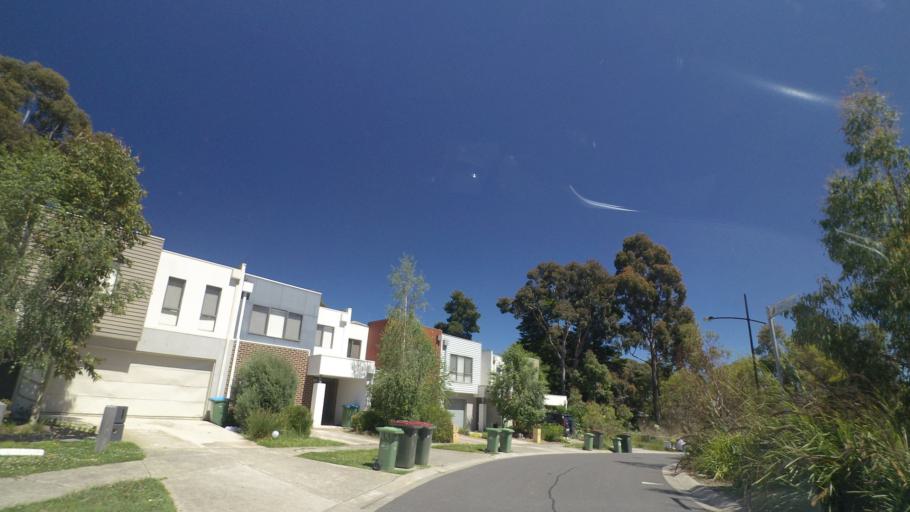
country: AU
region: Victoria
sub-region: Maroondah
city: Croydon North
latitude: -37.7836
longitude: 145.3004
